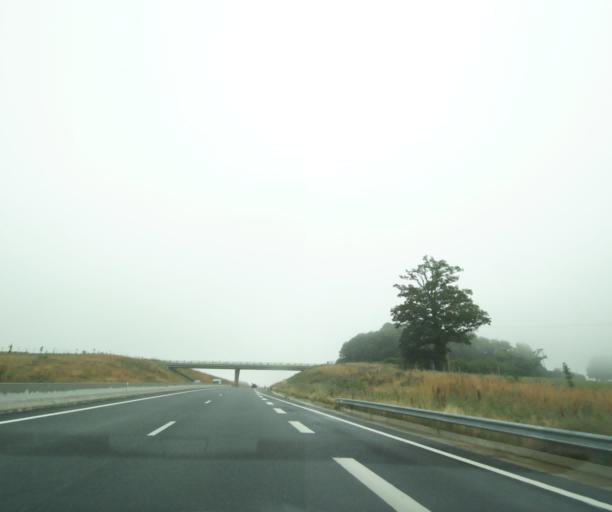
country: FR
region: Midi-Pyrenees
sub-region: Departement de l'Aveyron
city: Naucelle
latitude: 44.1460
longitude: 2.3216
